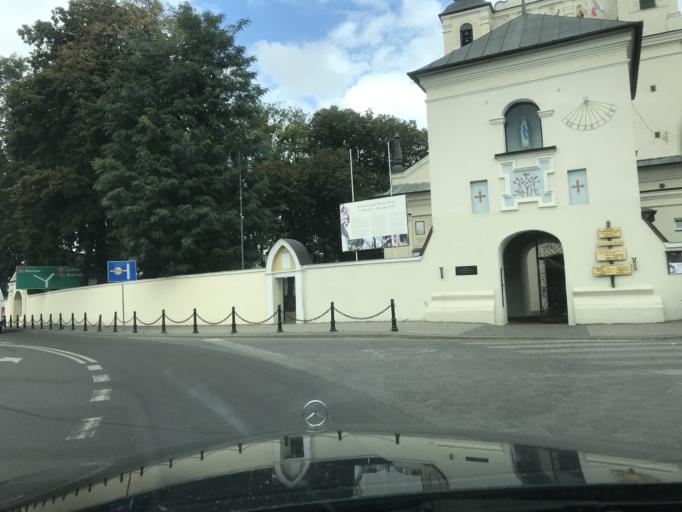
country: PL
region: Lublin Voivodeship
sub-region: Powiat janowski
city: Janow Lubelski
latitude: 50.7071
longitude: 22.4100
